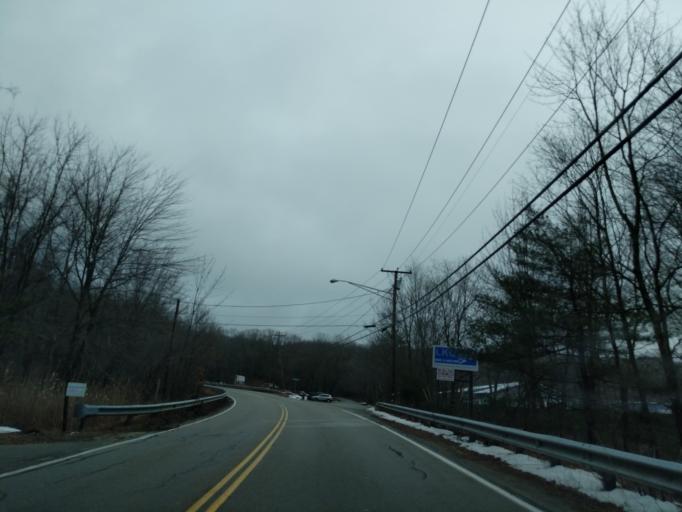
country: US
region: Massachusetts
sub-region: Worcester County
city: Webster
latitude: 42.0545
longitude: -71.8327
